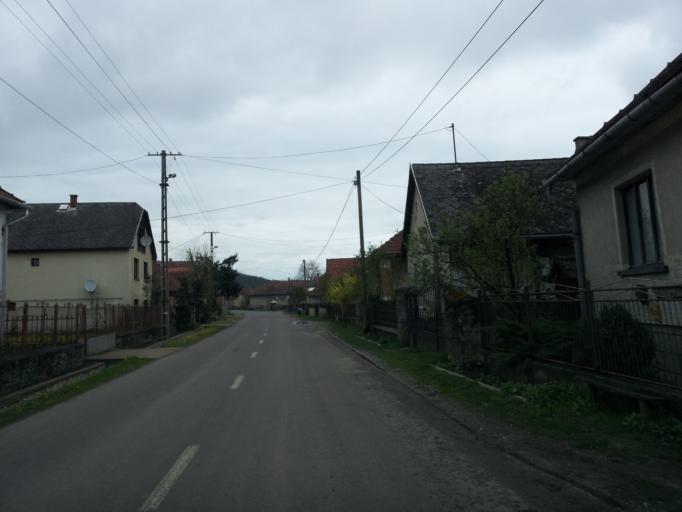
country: HU
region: Borsod-Abauj-Zemplen
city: Rudabanya
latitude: 48.4839
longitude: 20.6240
